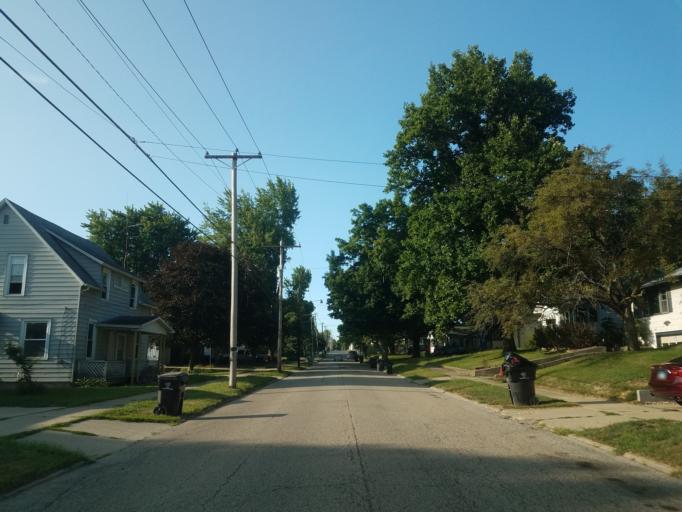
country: US
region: Illinois
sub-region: McLean County
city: Bloomington
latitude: 40.4920
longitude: -88.9818
